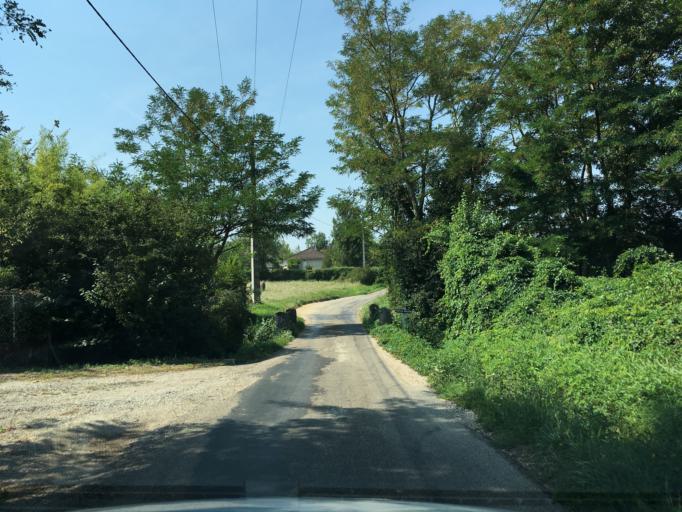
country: FR
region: Midi-Pyrenees
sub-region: Departement du Tarn-et-Garonne
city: Saint-Nauphary
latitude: 44.0047
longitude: 1.4072
